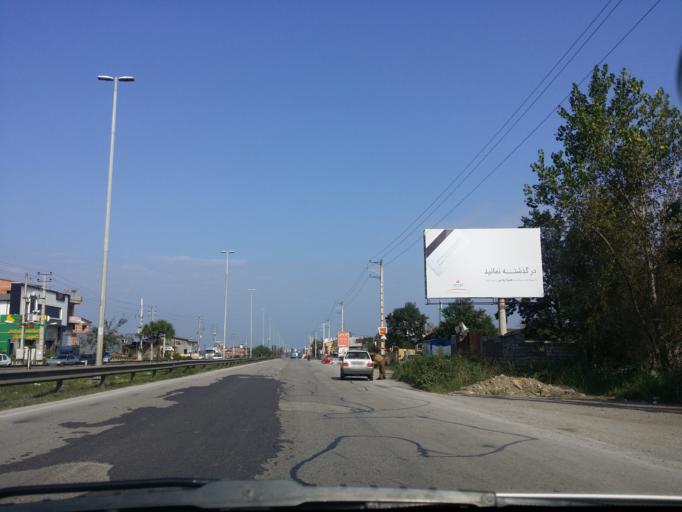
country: IR
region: Mazandaran
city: Chalus
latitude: 36.6644
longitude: 51.3981
